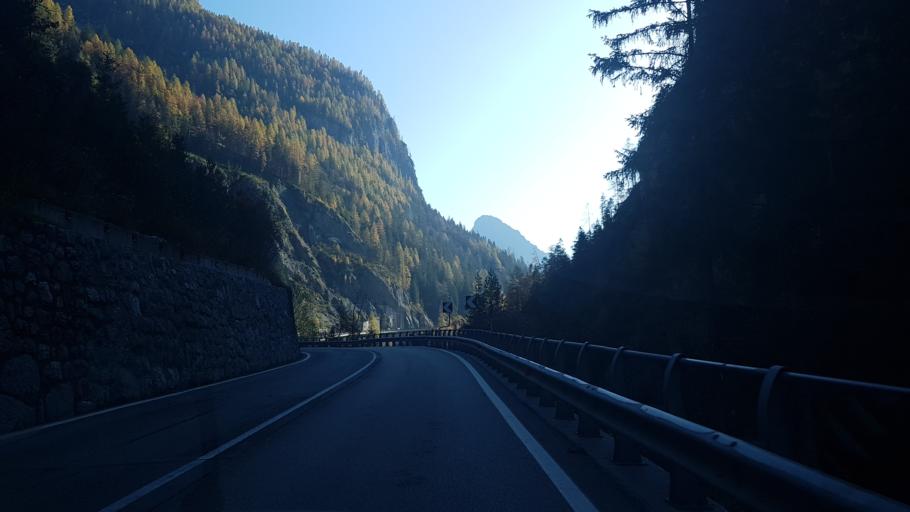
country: IT
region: Veneto
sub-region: Provincia di Belluno
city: Sappada
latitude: 46.5776
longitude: 12.6411
